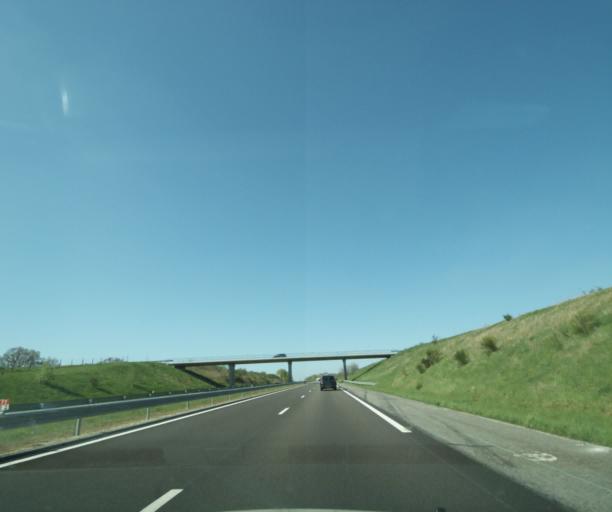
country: FR
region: Bourgogne
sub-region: Departement de la Nievre
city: Neuvy-sur-Loire
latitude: 47.4828
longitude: 2.9425
